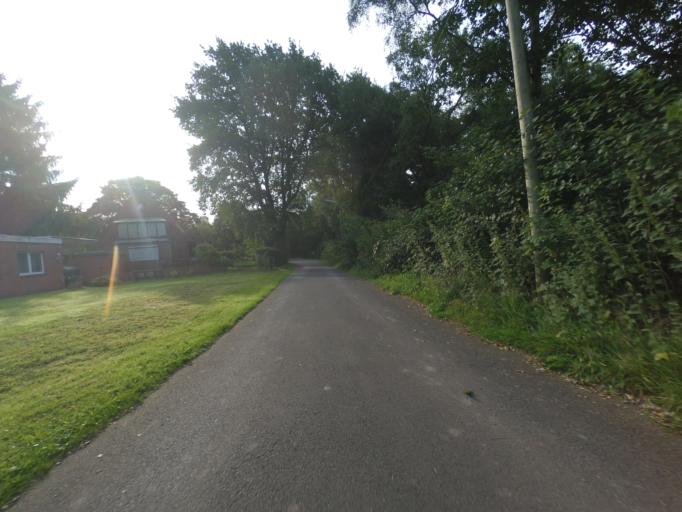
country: DE
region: Hamburg
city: Wandsbek
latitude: 53.5526
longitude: 10.1177
